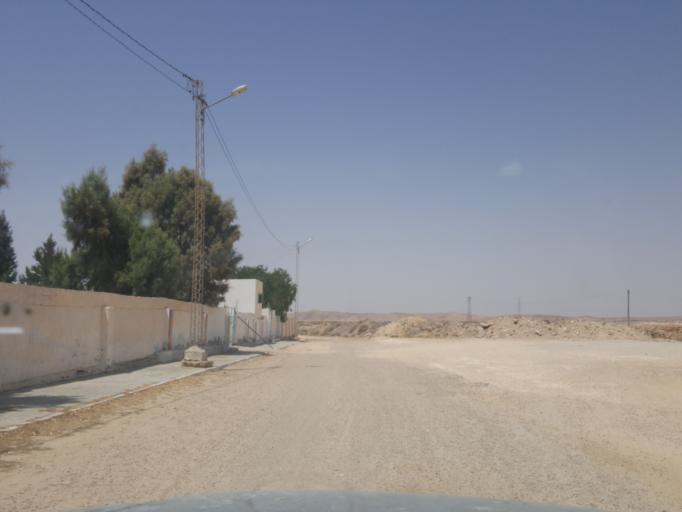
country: TN
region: Safaqis
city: Skhira
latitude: 34.1074
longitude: 9.9810
